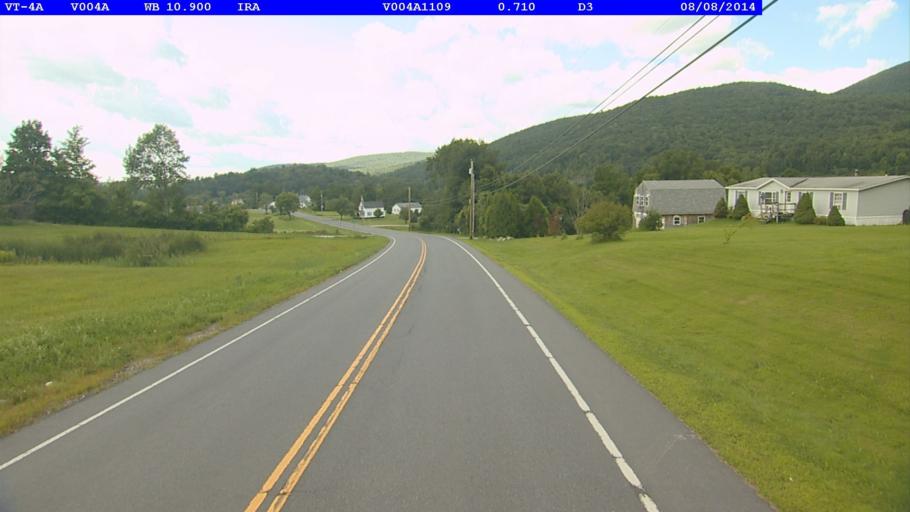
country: US
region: Vermont
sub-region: Rutland County
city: West Rutland
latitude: 43.6090
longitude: -73.0992
